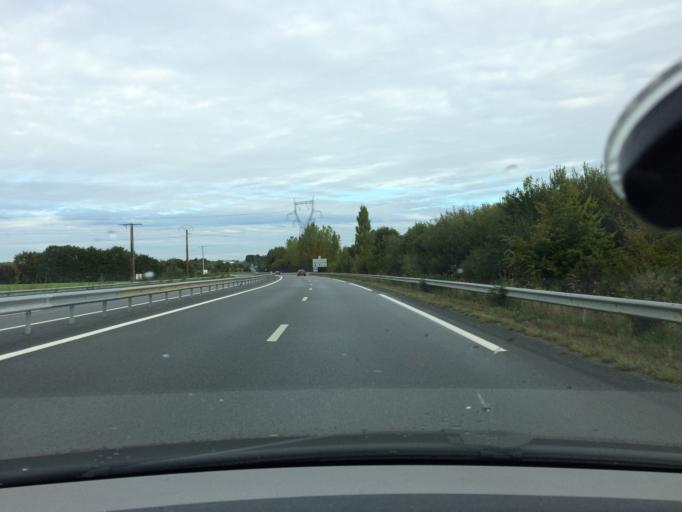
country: FR
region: Brittany
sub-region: Departement d'Ille-et-Vilaine
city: Janze
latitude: 47.9615
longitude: -1.5212
